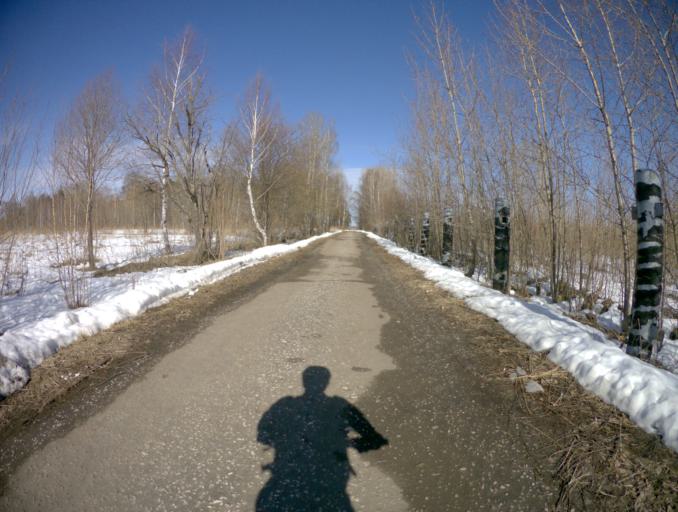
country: RU
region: Vladimir
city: Suzdal'
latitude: 56.4283
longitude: 40.4598
